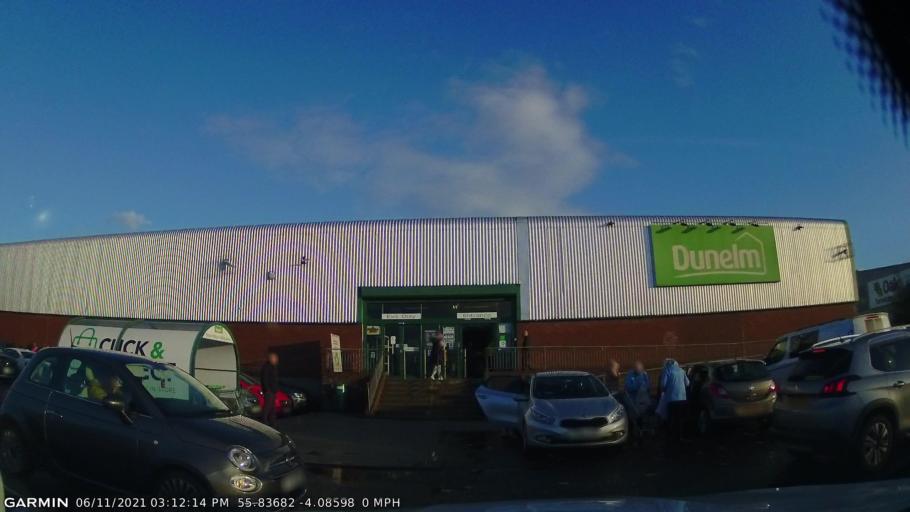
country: GB
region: Scotland
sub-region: South Lanarkshire
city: Uddingston
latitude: 55.8368
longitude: -4.0859
